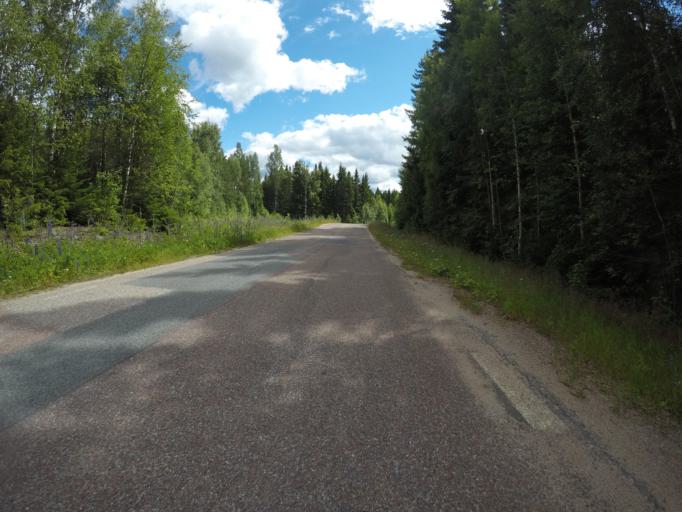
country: SE
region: OErebro
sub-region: Hallefors Kommun
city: Haellefors
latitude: 60.0549
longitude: 14.4987
